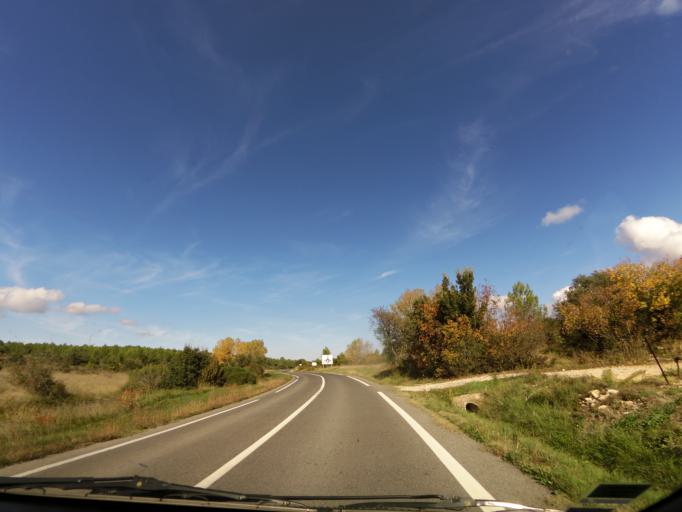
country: FR
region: Languedoc-Roussillon
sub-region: Departement du Gard
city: Villevieille
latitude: 43.8648
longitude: 4.0992
